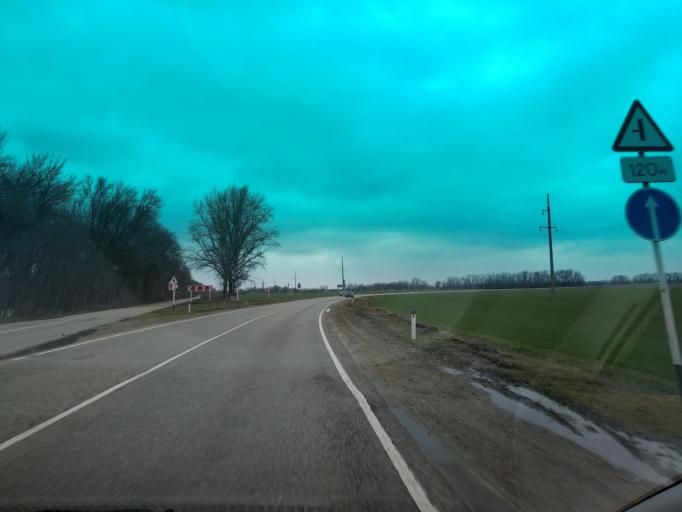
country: RU
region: Krasnodarskiy
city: Novorozhdestvenskaya
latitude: 45.7702
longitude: 39.9582
